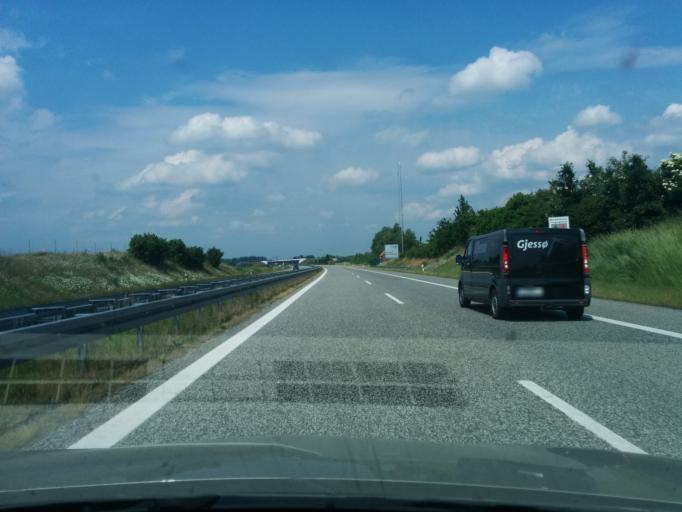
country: DE
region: Brandenburg
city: Schonfeld
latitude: 53.4340
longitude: 13.9952
